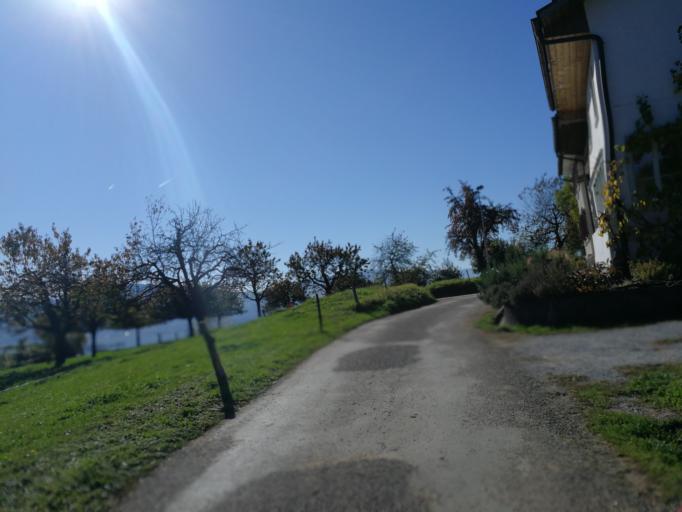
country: CH
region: Zurich
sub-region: Bezirk Hinwil
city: Wolfhausen
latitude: 47.2470
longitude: 8.8018
